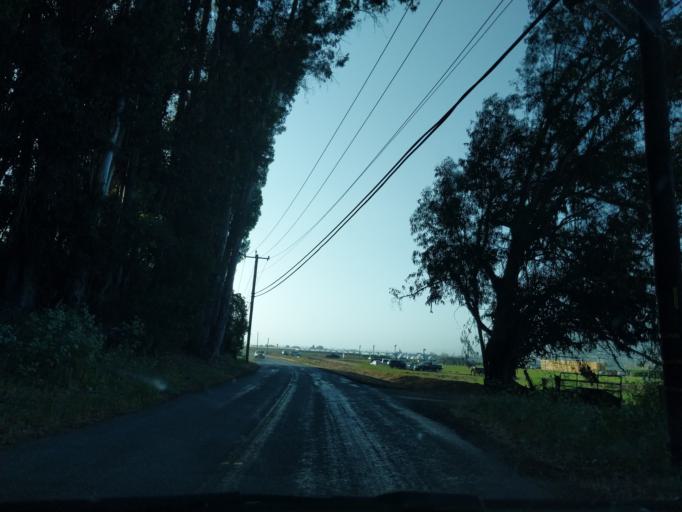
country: US
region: California
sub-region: San Benito County
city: Aromas
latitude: 36.8839
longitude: -121.6816
